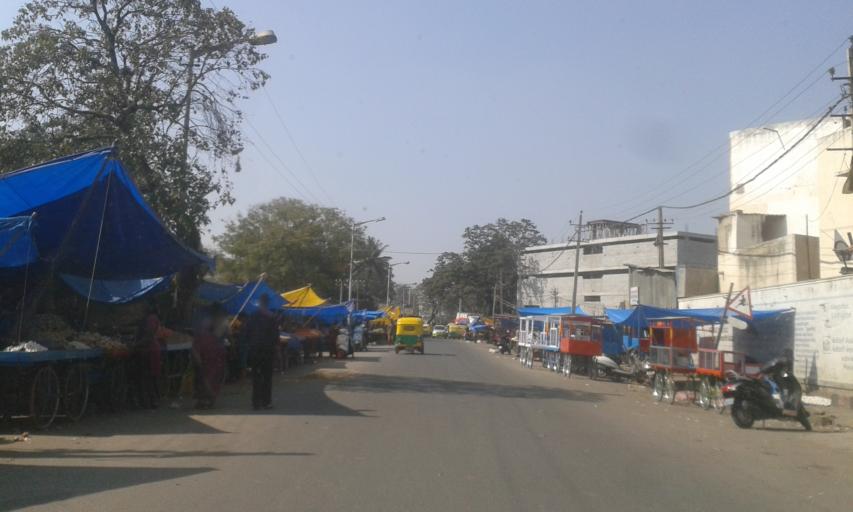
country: IN
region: Karnataka
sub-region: Bangalore Urban
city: Bangalore
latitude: 13.0201
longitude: 77.5541
